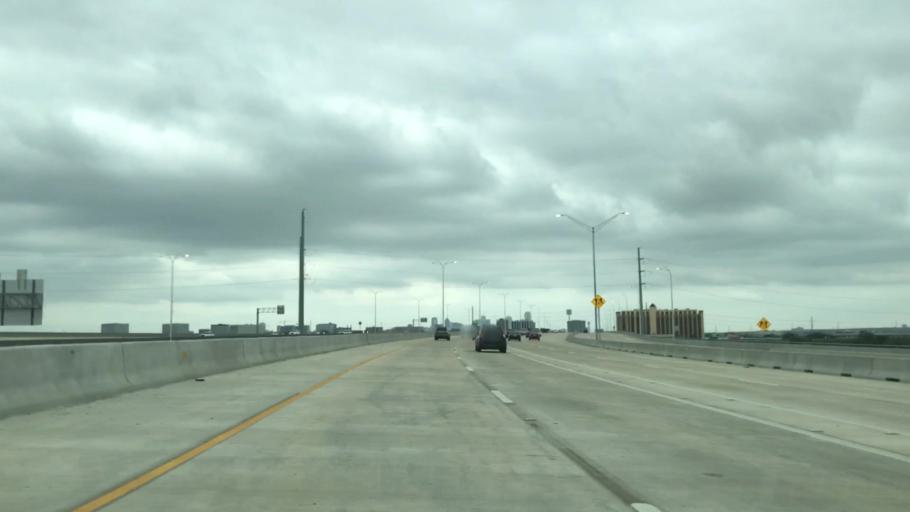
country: US
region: Texas
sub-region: Dallas County
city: Irving
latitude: 32.8327
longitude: -96.8945
